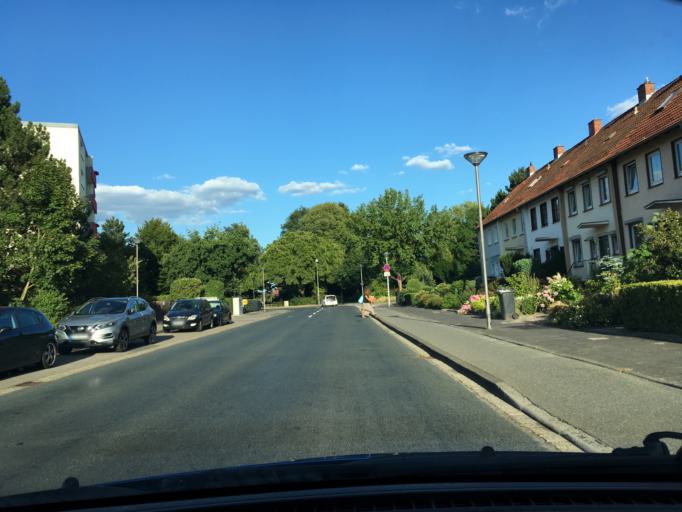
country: DE
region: Lower Saxony
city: Adelheidsdorf
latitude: 52.6046
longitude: 10.0349
